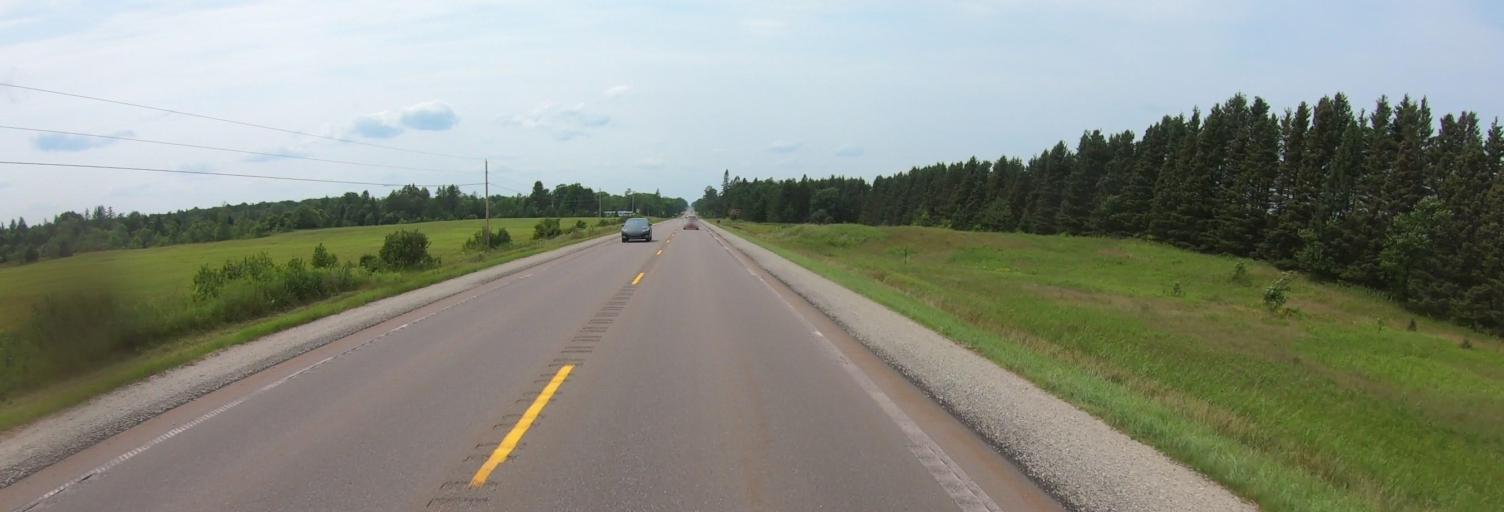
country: US
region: Michigan
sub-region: Marquette County
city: K. I. Sawyer Air Force Base
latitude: 46.3476
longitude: -87.0806
